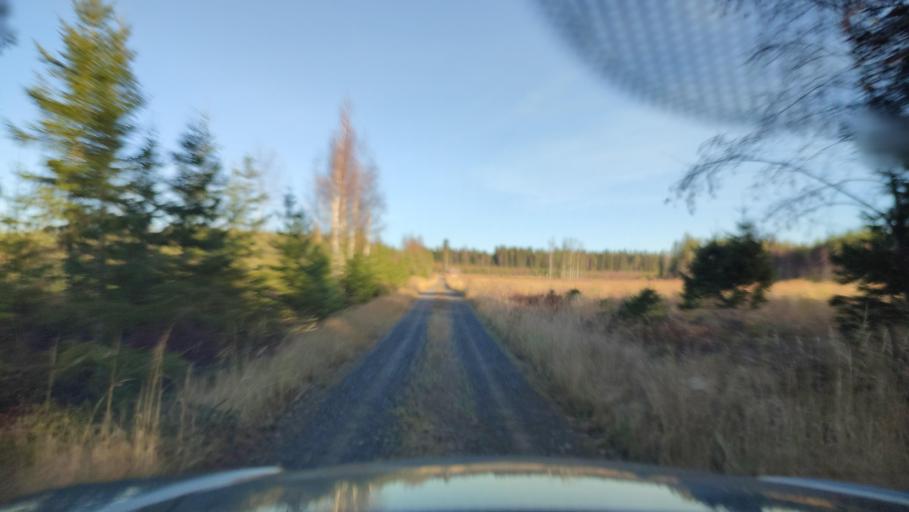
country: FI
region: Southern Ostrobothnia
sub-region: Suupohja
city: Karijoki
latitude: 62.1996
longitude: 21.6133
